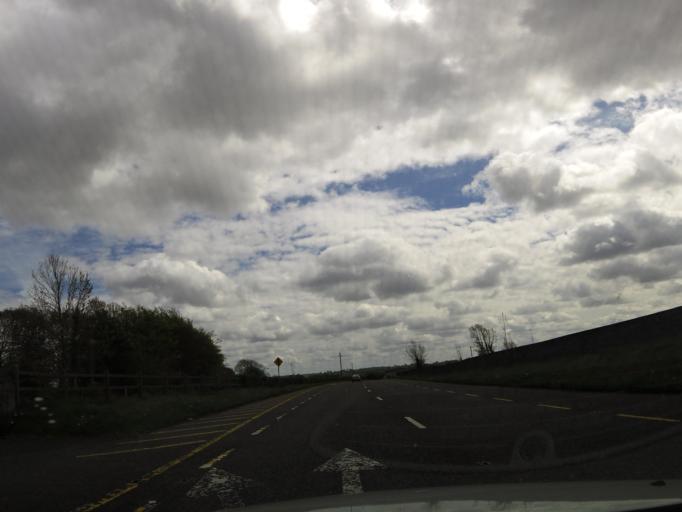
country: IE
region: Connaught
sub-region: County Galway
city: Tuam
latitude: 53.5942
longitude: -8.8714
